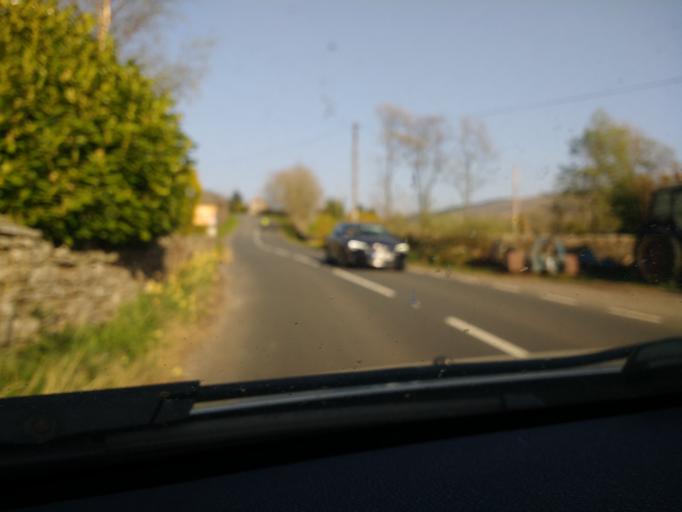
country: GB
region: England
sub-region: Cumbria
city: Sedbergh
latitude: 54.3065
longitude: -2.4220
